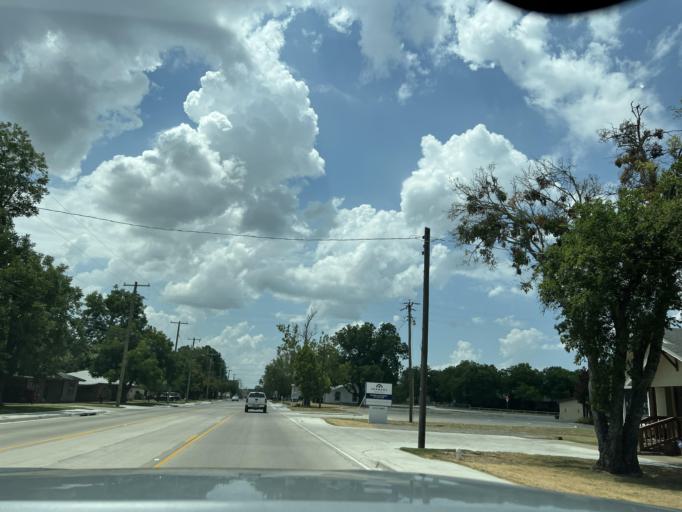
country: US
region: Texas
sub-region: Parker County
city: Springtown
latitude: 32.9699
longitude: -97.6847
